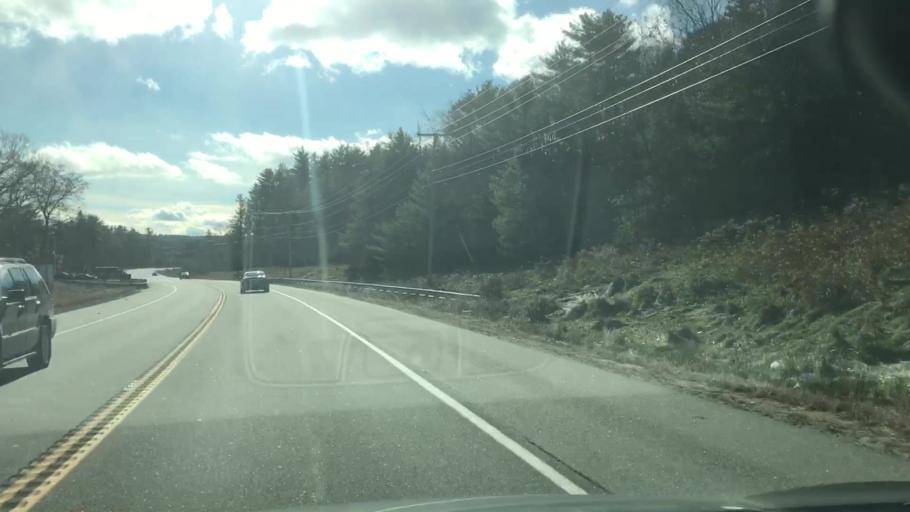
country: US
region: New Hampshire
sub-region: Belknap County
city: Barnstead
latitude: 43.3248
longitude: -71.3051
